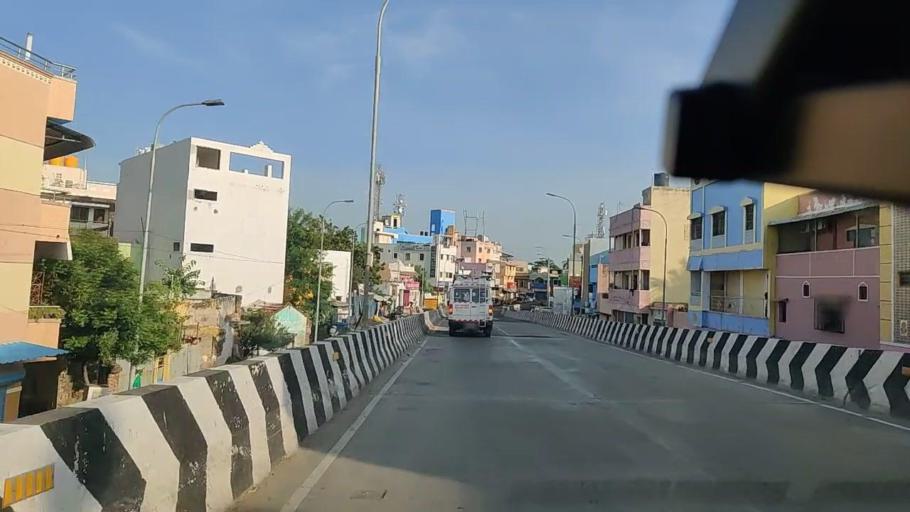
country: IN
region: Tamil Nadu
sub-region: Chennai
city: George Town
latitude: 13.1126
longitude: 80.2643
